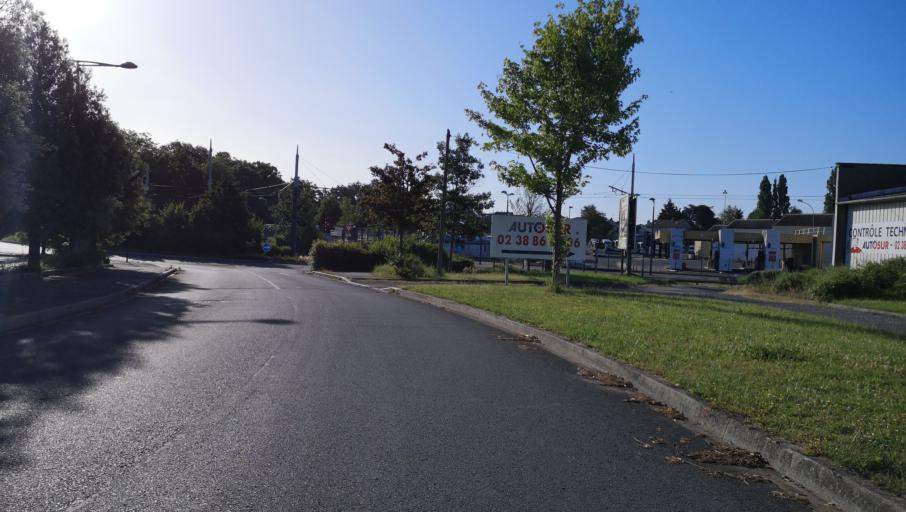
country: FR
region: Centre
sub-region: Departement du Loiret
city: Semoy
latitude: 47.9105
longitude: 1.9439
